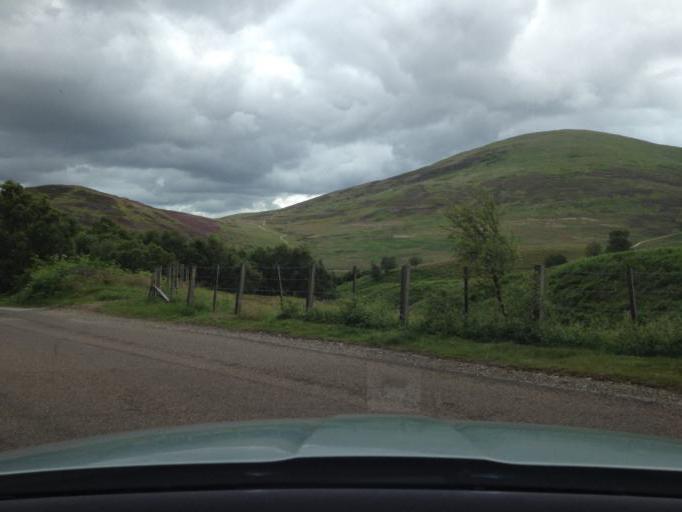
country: GB
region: Scotland
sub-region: Aberdeenshire
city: Aboyne
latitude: 56.8909
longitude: -2.7764
